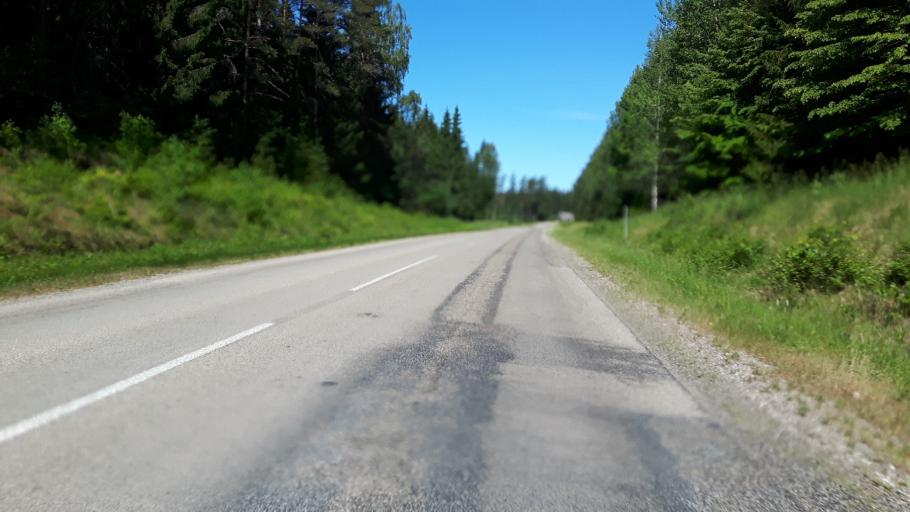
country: LV
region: Tukuma Rajons
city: Tukums
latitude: 57.0086
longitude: 23.0575
